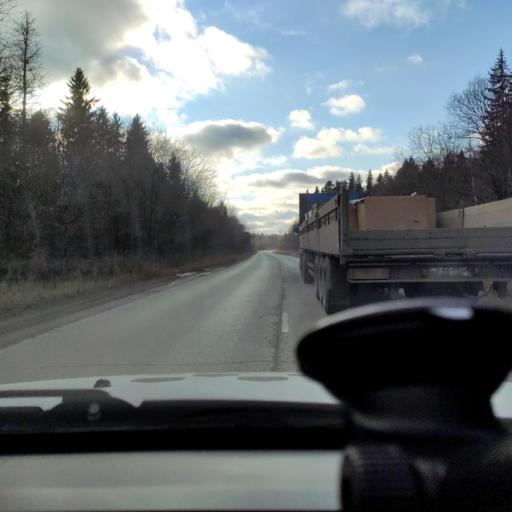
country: RU
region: Perm
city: Ferma
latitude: 57.9622
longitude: 56.3480
